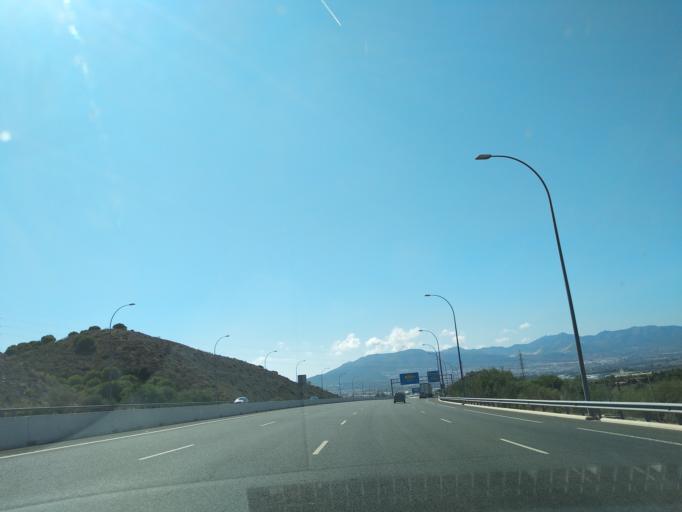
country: ES
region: Andalusia
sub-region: Provincia de Malaga
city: Alhaurin de la Torre
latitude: 36.7281
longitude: -4.5070
